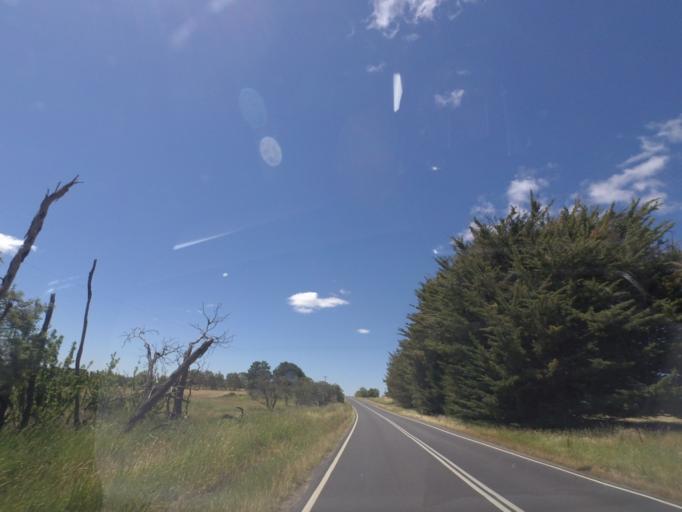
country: AU
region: Victoria
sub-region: Mount Alexander
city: Castlemaine
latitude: -37.2425
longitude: 144.3253
